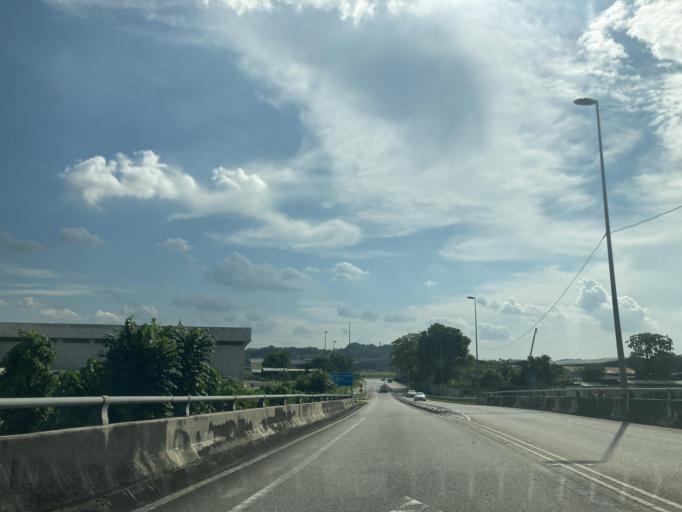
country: MY
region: Selangor
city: Kampung Baru Subang
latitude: 3.1400
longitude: 101.5505
